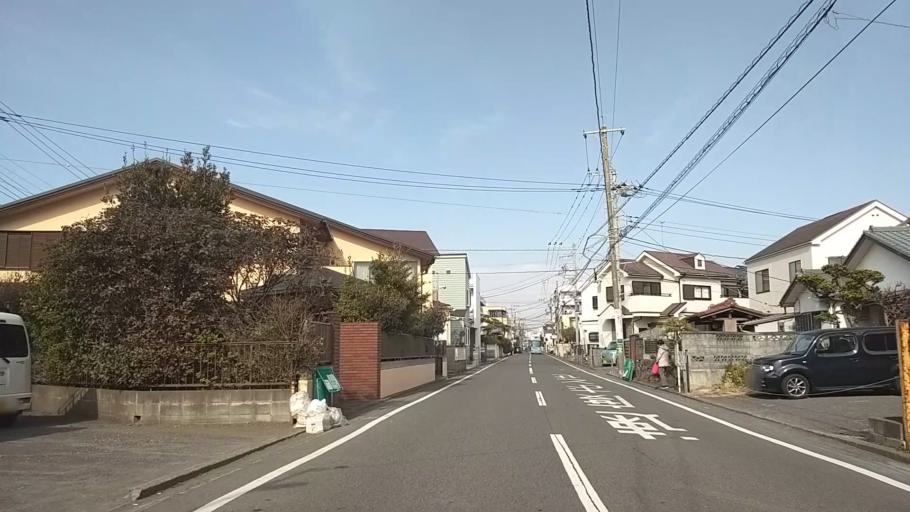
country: JP
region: Kanagawa
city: Chigasaki
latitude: 35.3216
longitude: 139.4000
